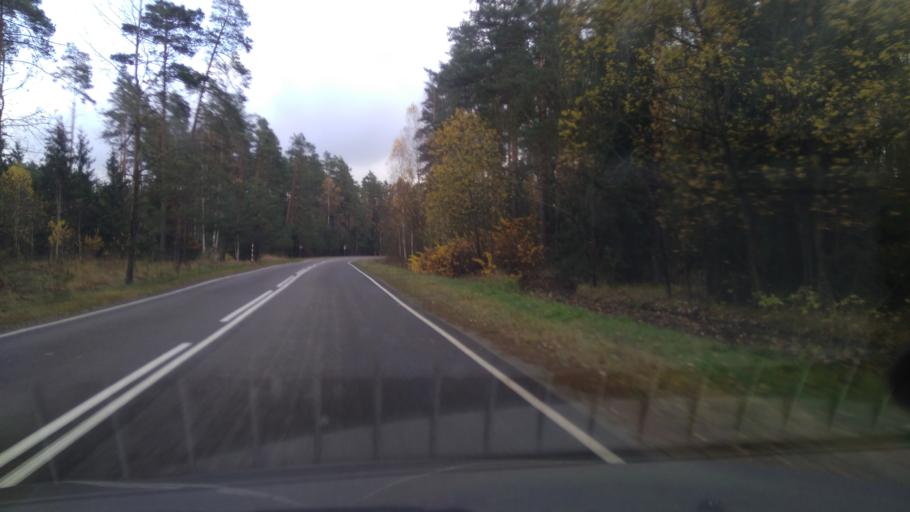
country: BY
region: Minsk
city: Slutsk
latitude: 53.2284
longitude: 27.7318
